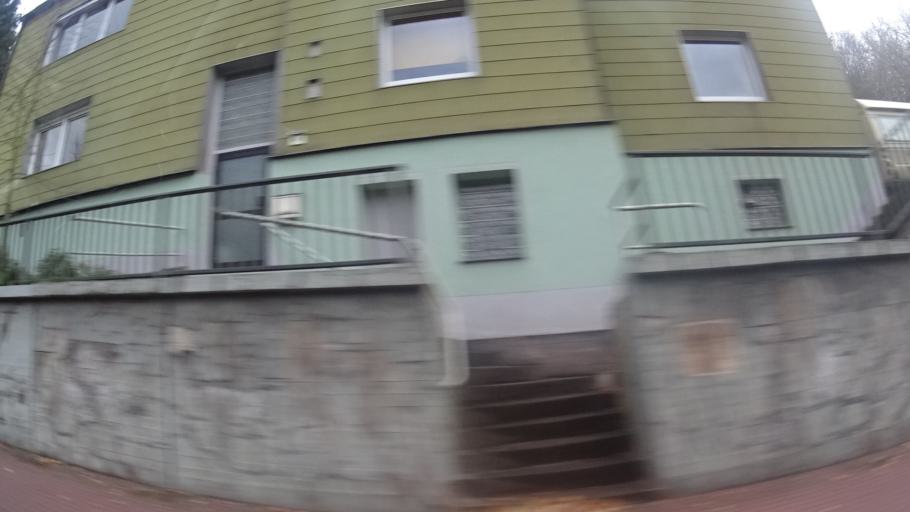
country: DE
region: Thuringia
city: Unterbreizbach
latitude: 50.8455
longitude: 9.9438
